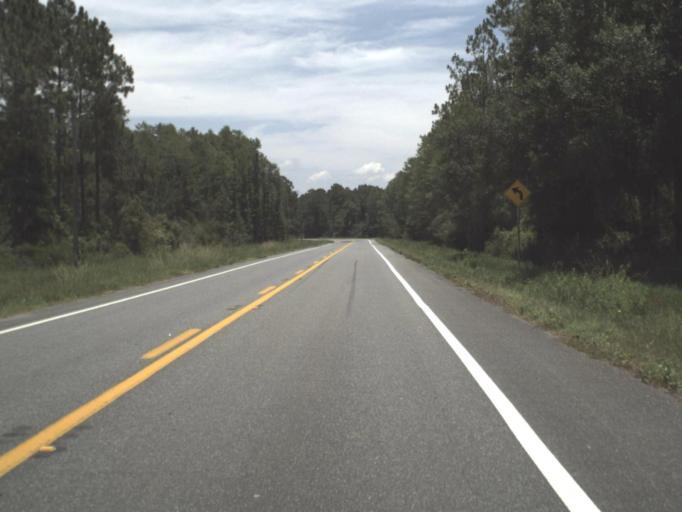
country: US
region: Florida
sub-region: Lafayette County
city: Mayo
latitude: 30.0381
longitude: -83.1777
